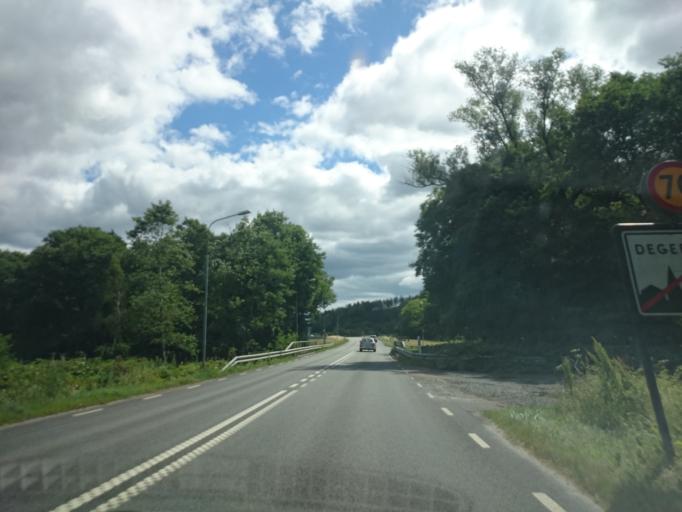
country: SE
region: Skane
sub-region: Kristianstads Kommun
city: Degeberga
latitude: 55.8275
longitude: 14.0947
